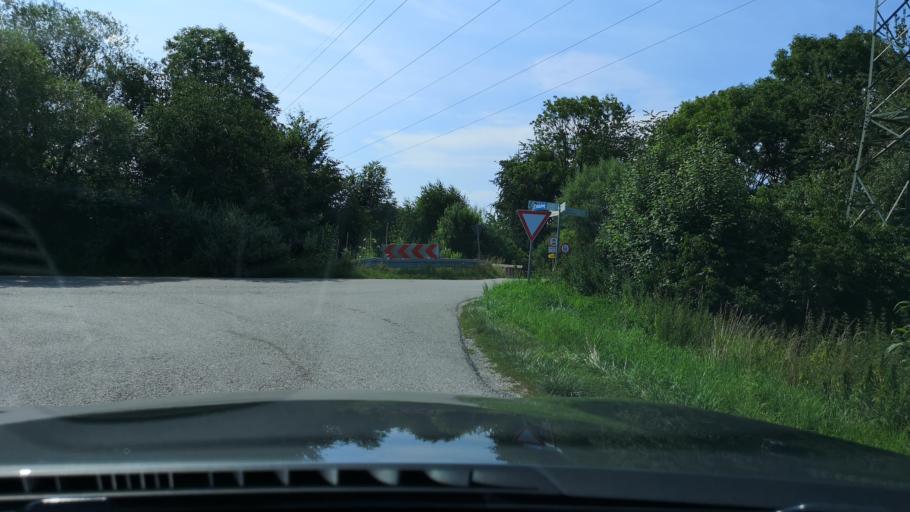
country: DE
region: Bavaria
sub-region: Upper Bavaria
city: Kirchheim bei Muenchen
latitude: 48.2082
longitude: 11.7682
